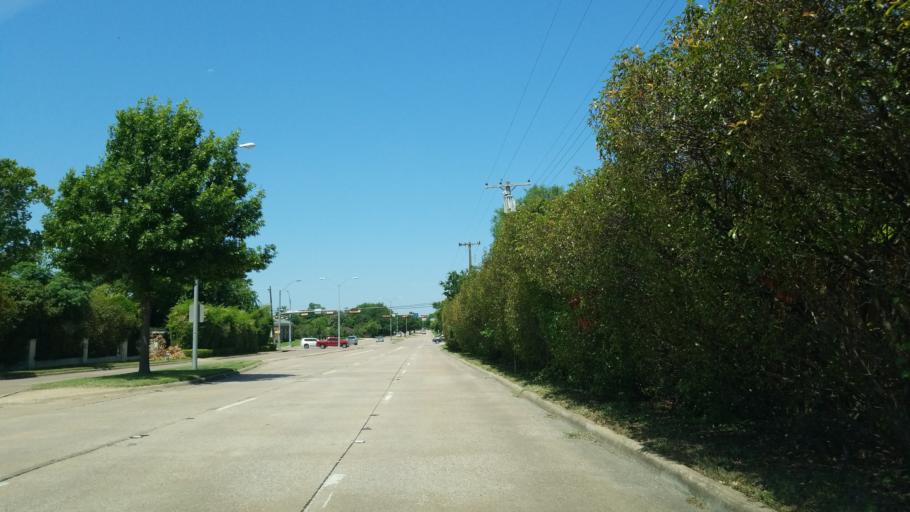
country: US
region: Texas
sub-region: Dallas County
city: University Park
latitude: 32.8951
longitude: -96.8369
